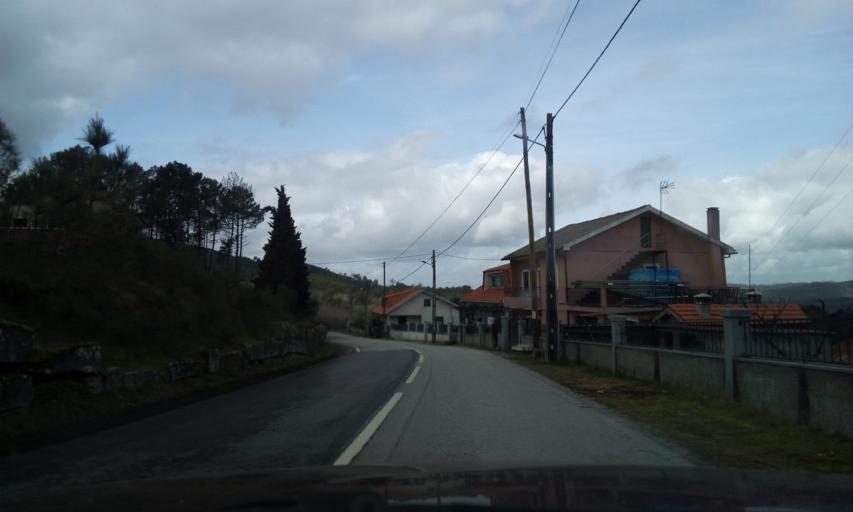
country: PT
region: Guarda
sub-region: Fornos de Algodres
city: Fornos de Algodres
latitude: 40.6634
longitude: -7.6011
